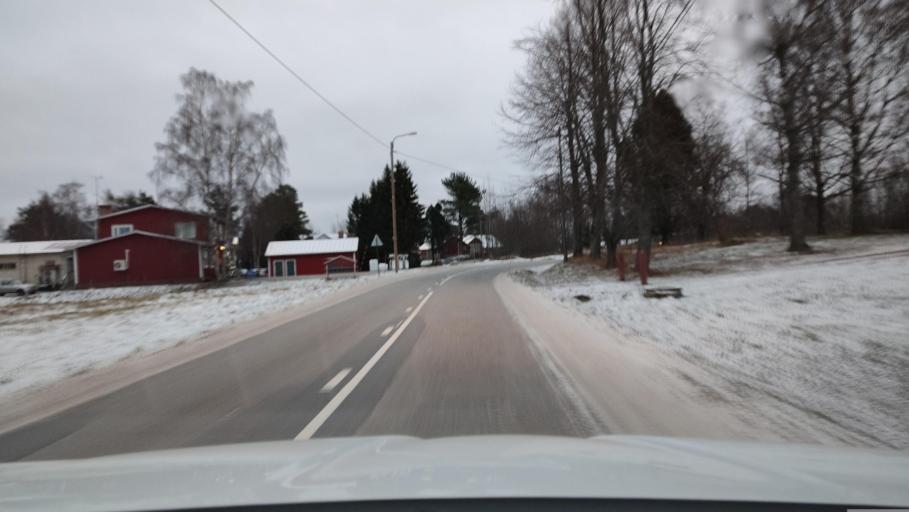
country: FI
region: Ostrobothnia
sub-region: Vaasa
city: Replot
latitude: 63.3451
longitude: 21.3213
